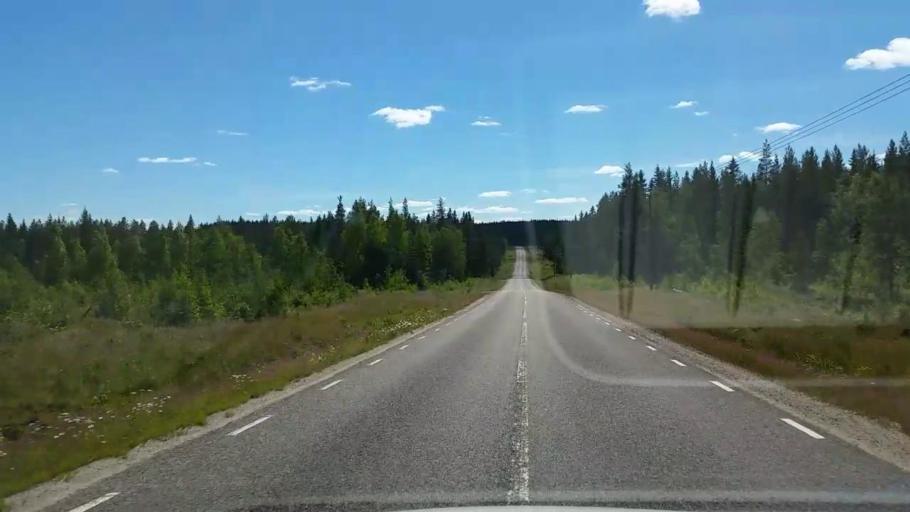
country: SE
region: Gaevleborg
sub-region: Ovanakers Kommun
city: Edsbyn
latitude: 61.5373
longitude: 15.6810
